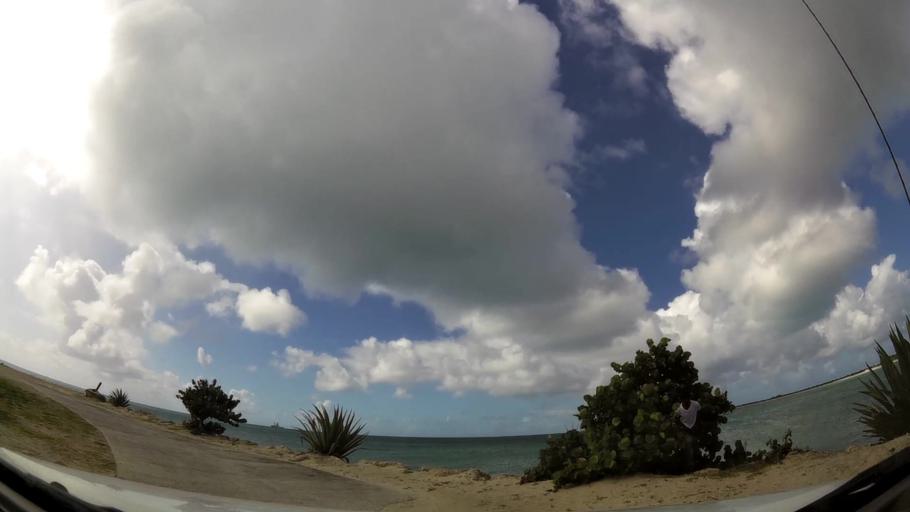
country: AG
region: Barbuda
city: Codrington
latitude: 17.5905
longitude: -61.8216
